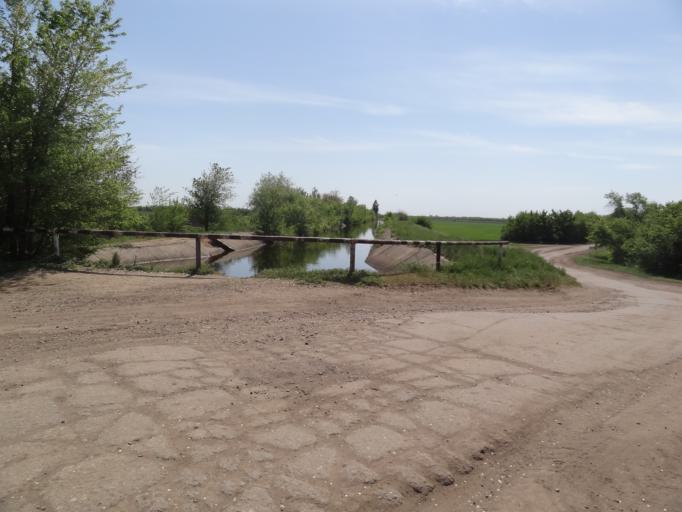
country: RU
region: Saratov
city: Engel's
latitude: 51.3597
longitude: 46.2070
